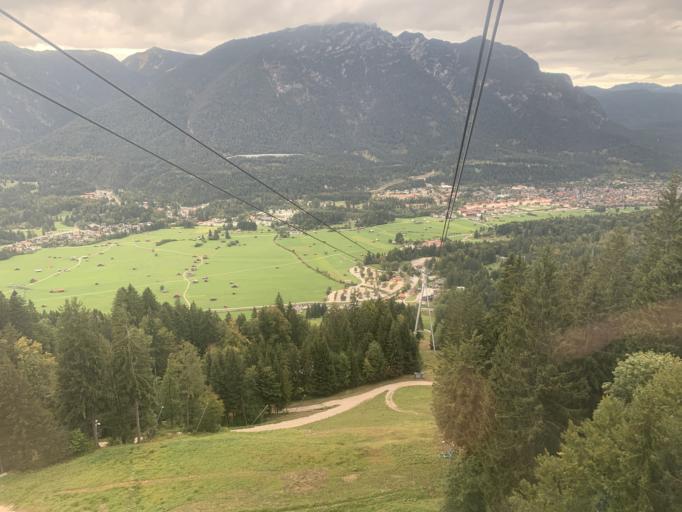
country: DE
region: Bavaria
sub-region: Upper Bavaria
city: Garmisch-Partenkirchen
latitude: 47.4633
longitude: 11.0652
